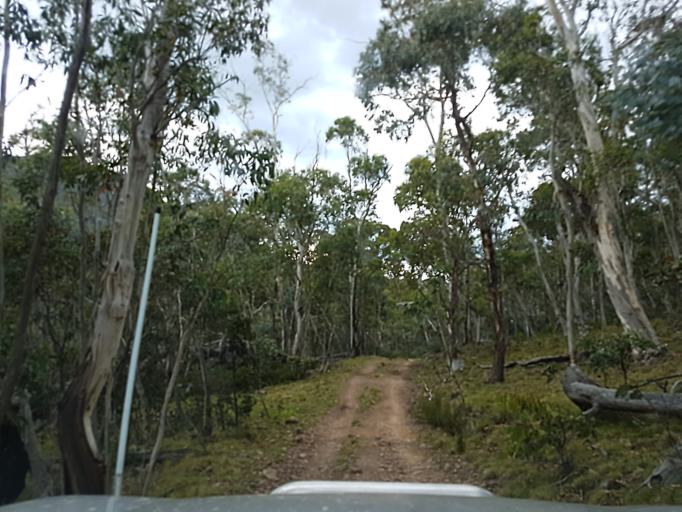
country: AU
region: New South Wales
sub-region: Snowy River
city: Jindabyne
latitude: -36.8834
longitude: 148.1484
